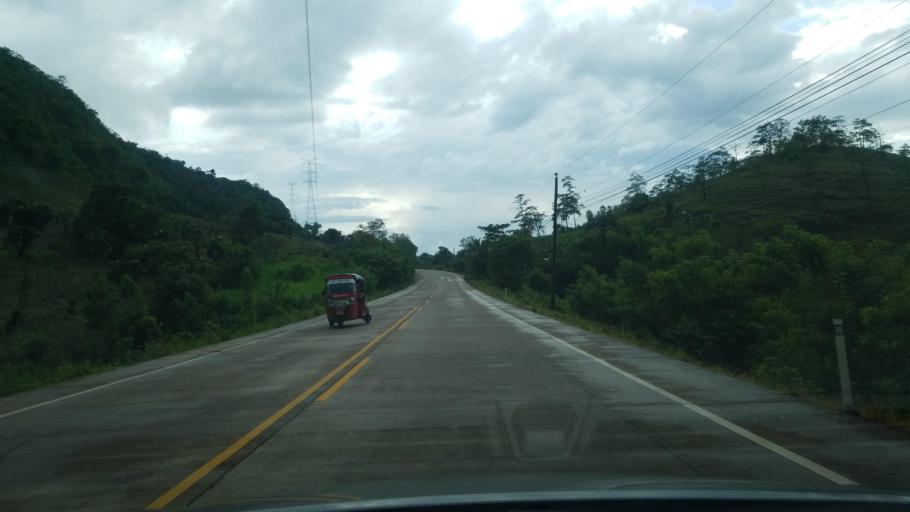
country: HN
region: Copan
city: Copan
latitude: 14.8557
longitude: -89.2011
